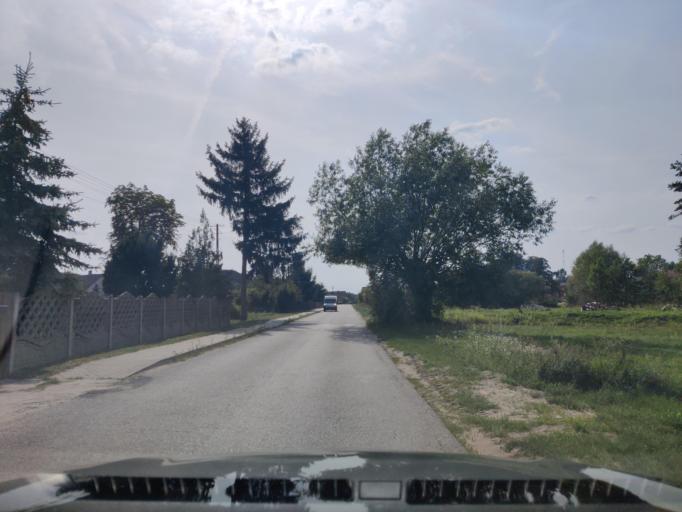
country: PL
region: Masovian Voivodeship
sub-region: Powiat wyszkowski
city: Rzasnik
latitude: 52.7639
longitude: 21.3569
